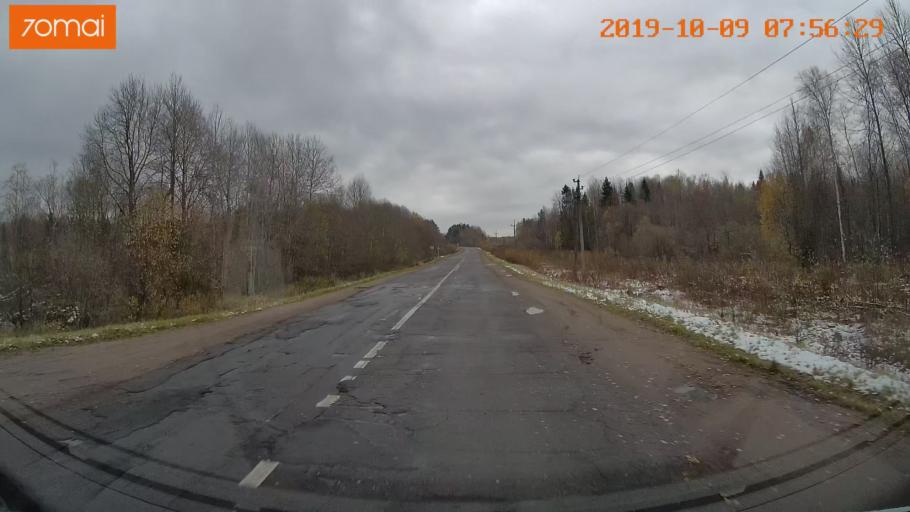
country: RU
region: Jaroslavl
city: Kukoboy
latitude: 58.6979
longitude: 39.9358
